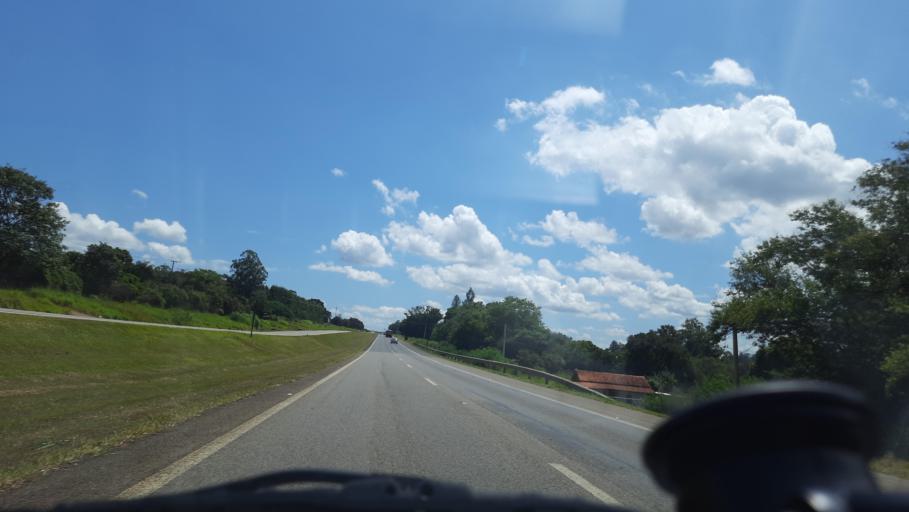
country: BR
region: Sao Paulo
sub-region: Moji-Guacu
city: Mogi-Gaucu
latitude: -22.2407
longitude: -46.9781
